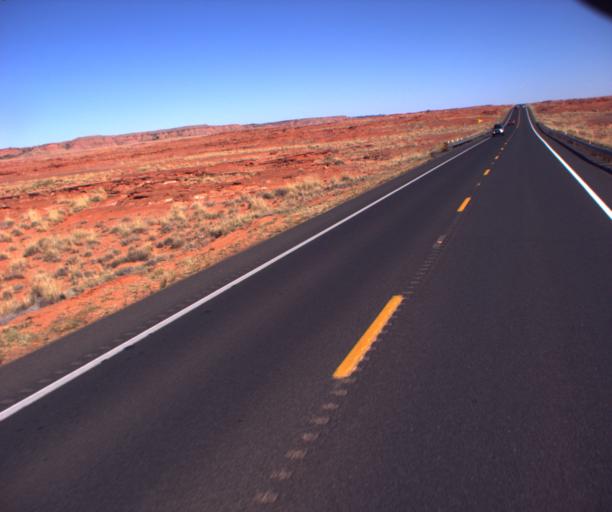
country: US
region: Arizona
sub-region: Coconino County
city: Tuba City
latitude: 36.0995
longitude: -111.3307
